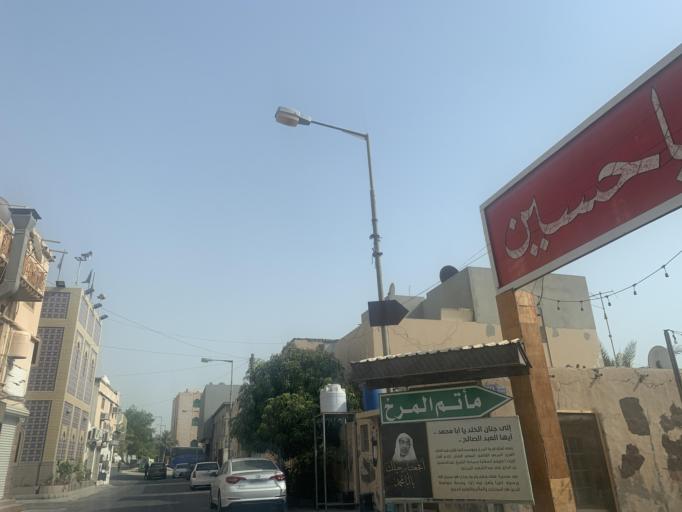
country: BH
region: Manama
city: Jidd Hafs
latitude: 26.2108
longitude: 50.4740
